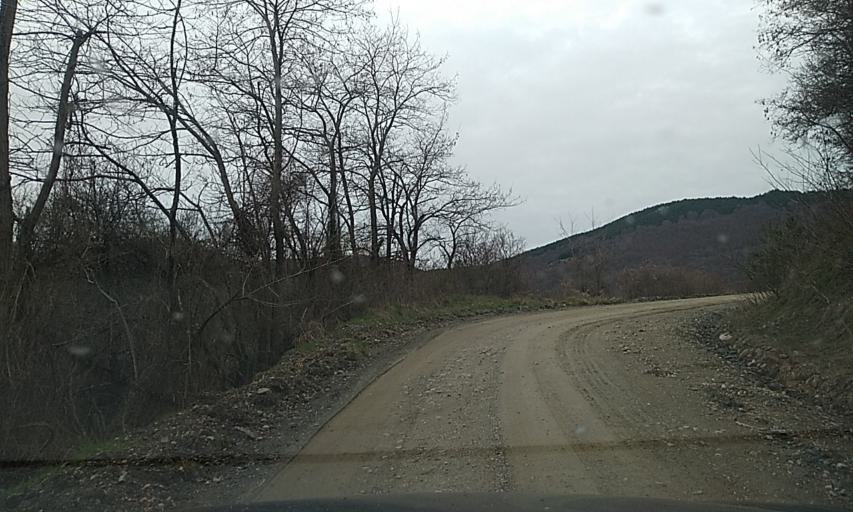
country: MK
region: Kriva Palanka
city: Kriva Palanka
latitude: 42.3420
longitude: 22.3557
